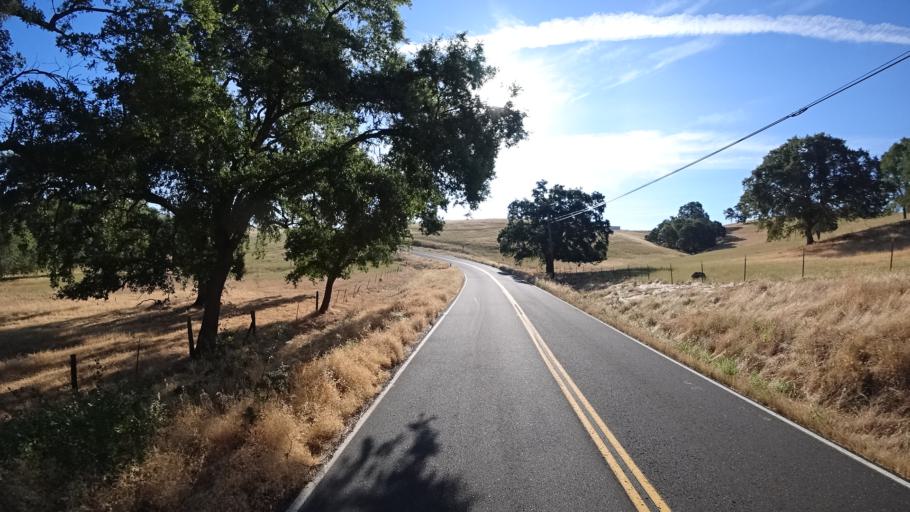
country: US
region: California
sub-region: Calaveras County
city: Valley Springs
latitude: 38.2143
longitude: -120.7718
